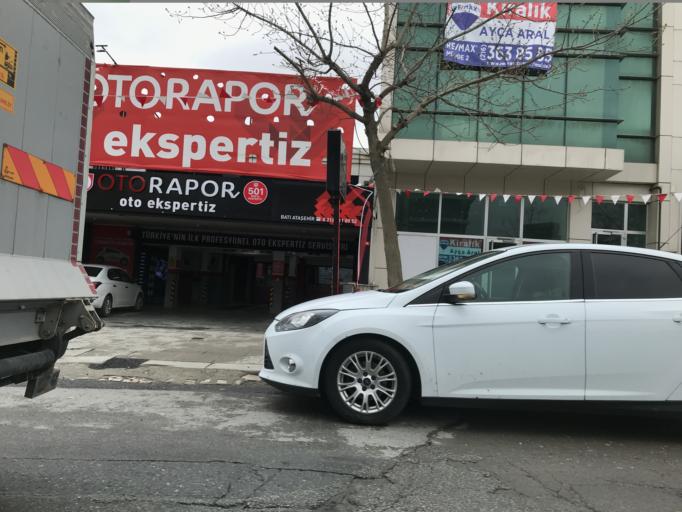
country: TR
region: Istanbul
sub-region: Atasehir
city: Atasehir
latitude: 40.9851
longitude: 29.0979
